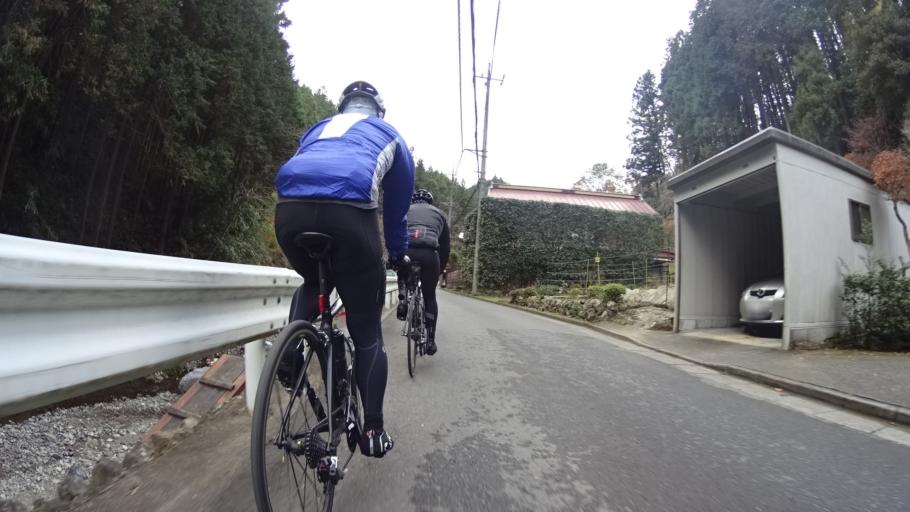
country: JP
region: Saitama
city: Morohongo
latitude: 35.9231
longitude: 139.1903
